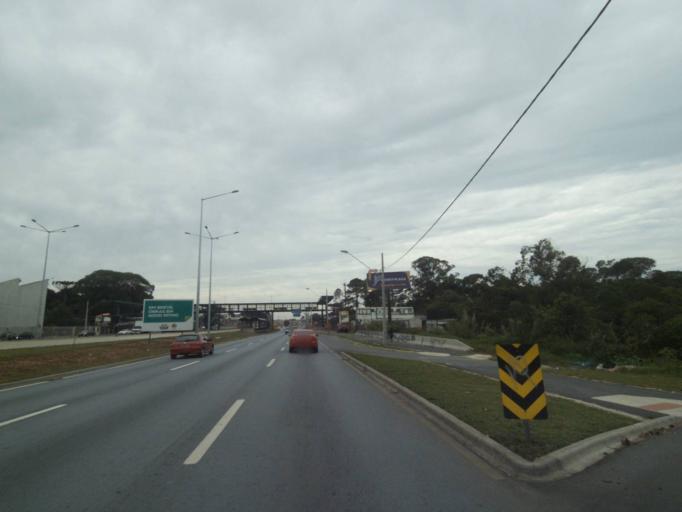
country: BR
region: Parana
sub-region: Pinhais
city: Pinhais
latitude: -25.4214
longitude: -49.2252
